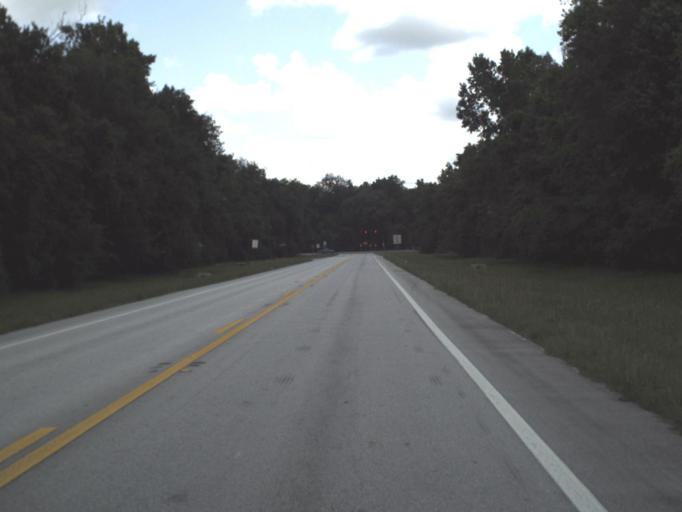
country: US
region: Florida
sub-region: Hernando County
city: North Brooksville
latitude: 28.6114
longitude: -82.4070
